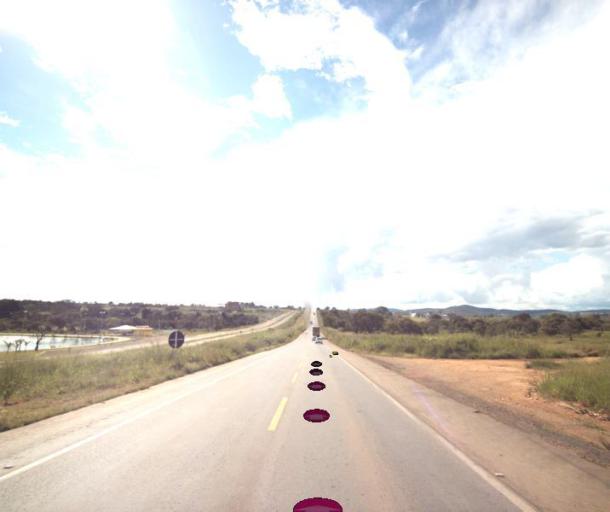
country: BR
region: Goias
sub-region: Jaragua
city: Jaragua
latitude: -15.7488
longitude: -49.3175
